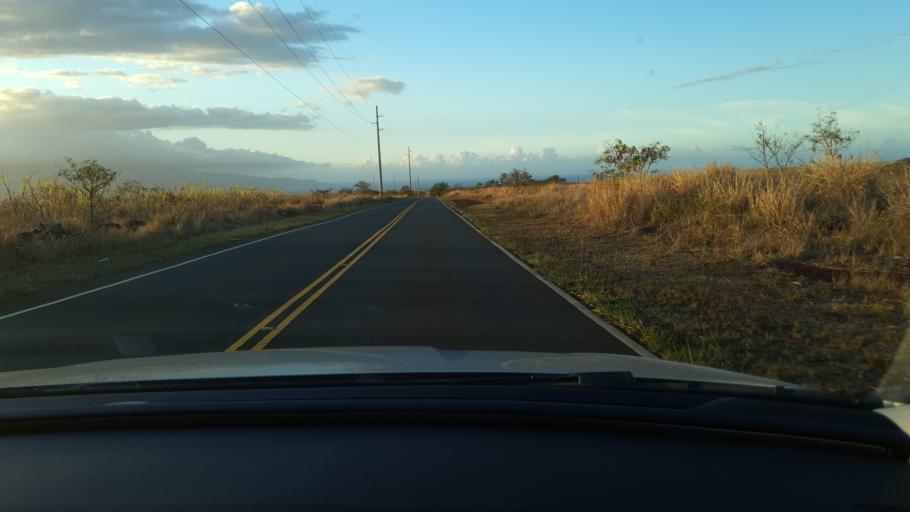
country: US
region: Hawaii
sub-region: Maui County
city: Pukalani
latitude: 20.8098
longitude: -156.3816
